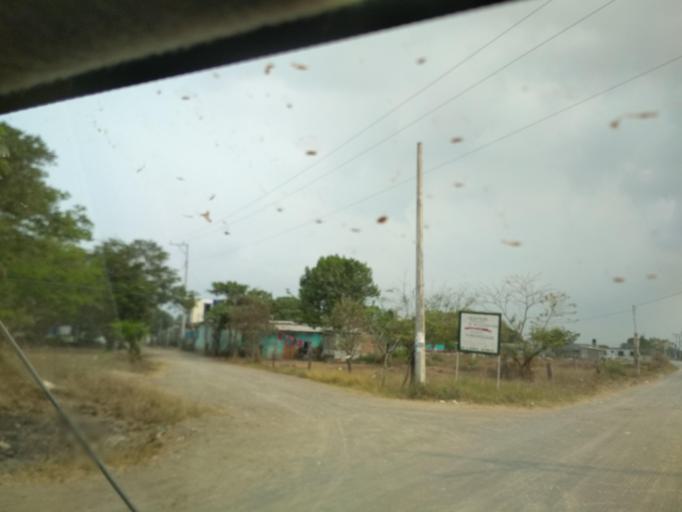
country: MX
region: Veracruz
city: Paso del Toro
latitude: 19.0103
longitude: -96.1111
